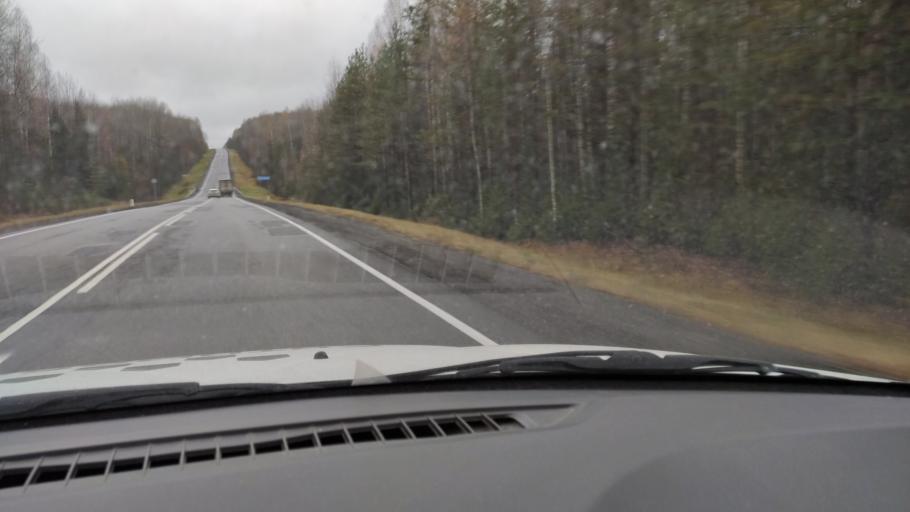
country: RU
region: Kirov
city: Chernaya Kholunitsa
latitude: 58.8589
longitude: 51.6274
